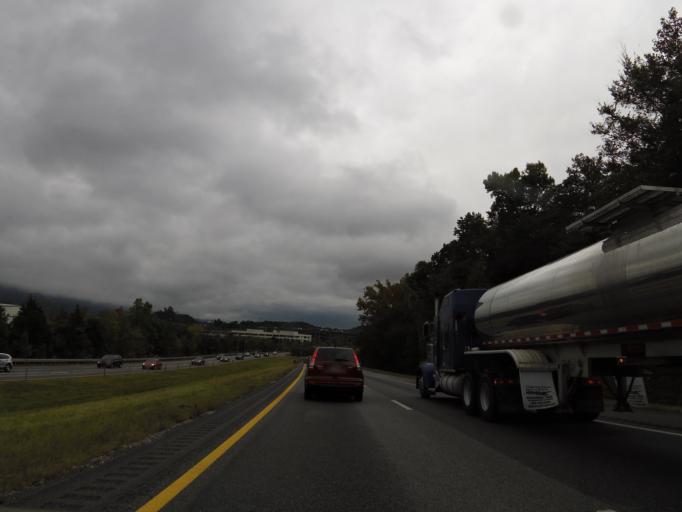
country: US
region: Tennessee
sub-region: Hamilton County
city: Lookout Mountain
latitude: 35.0144
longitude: -85.3878
